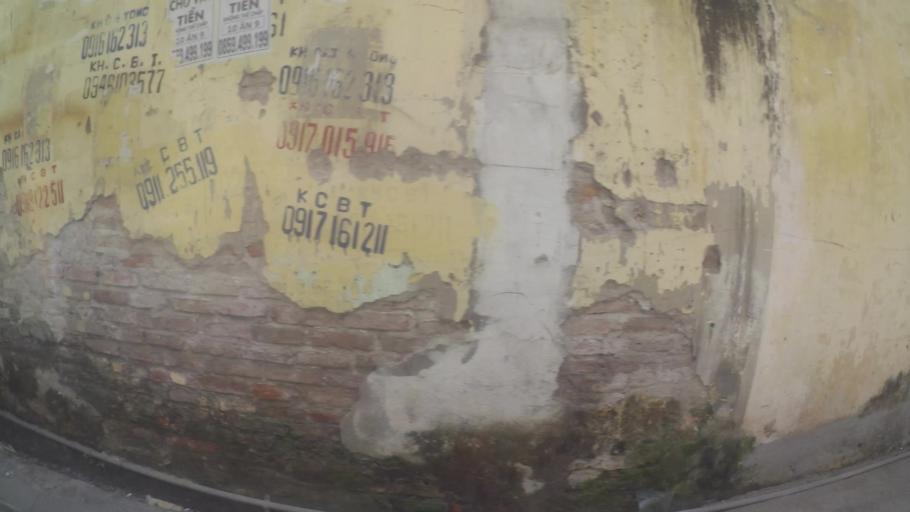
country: VN
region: Ha Noi
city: Ha Dong
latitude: 20.9718
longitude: 105.7660
